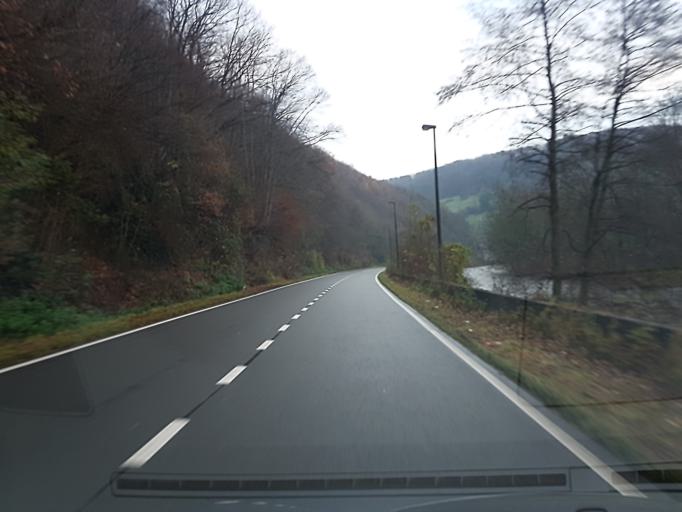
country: BE
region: Wallonia
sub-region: Province de Liege
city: Olne
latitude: 50.5755
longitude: 5.7613
